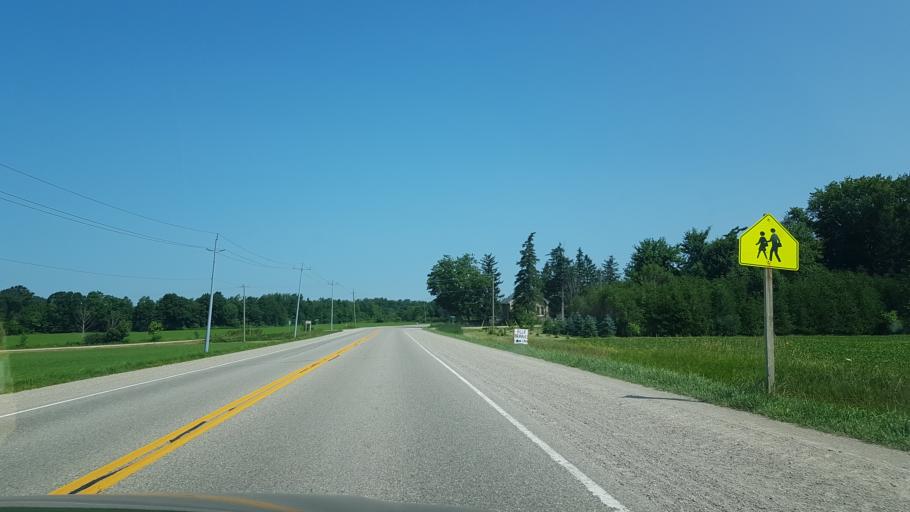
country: CA
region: Ontario
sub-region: Oxford County
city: Woodstock
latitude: 42.9439
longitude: -80.6790
